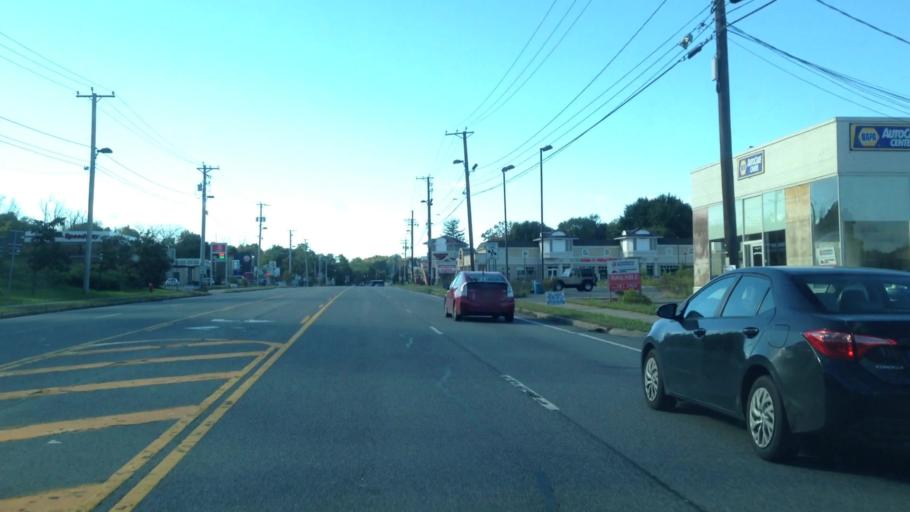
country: US
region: New York
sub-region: Ulster County
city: Highland
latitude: 41.7156
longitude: -73.9633
